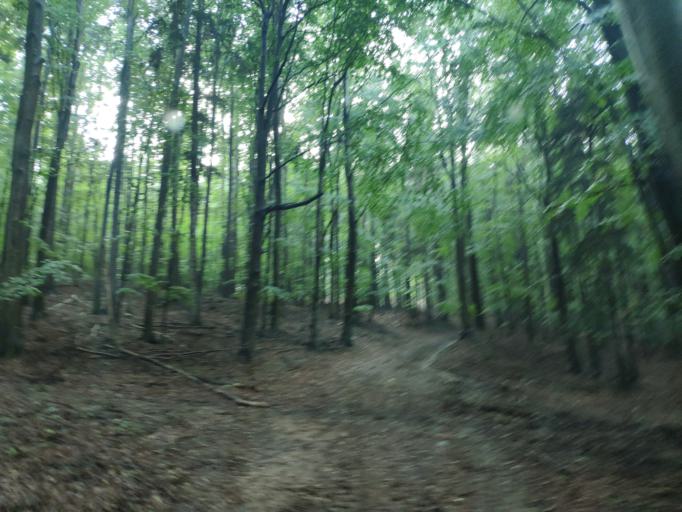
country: SK
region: Kosicky
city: Medzev
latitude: 48.7494
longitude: 20.9935
